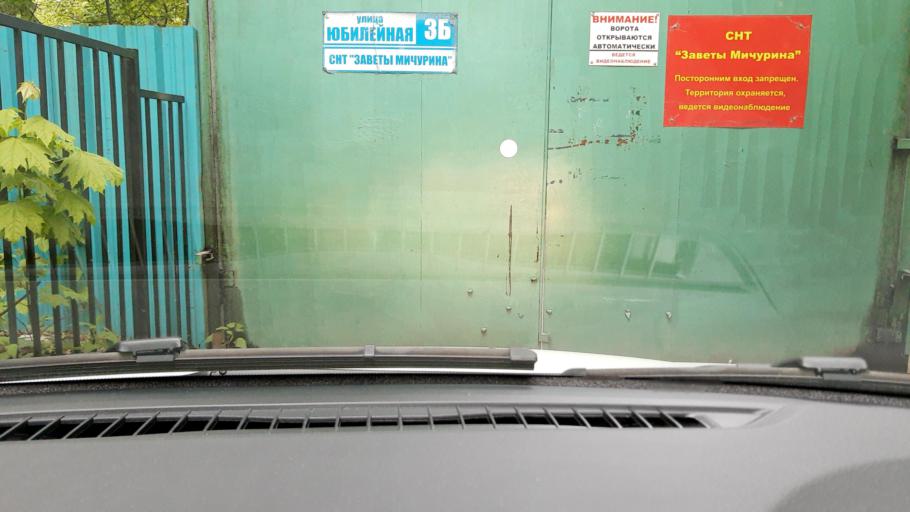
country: RU
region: Nizjnij Novgorod
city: Nizhniy Novgorod
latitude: 56.2807
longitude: 44.0069
